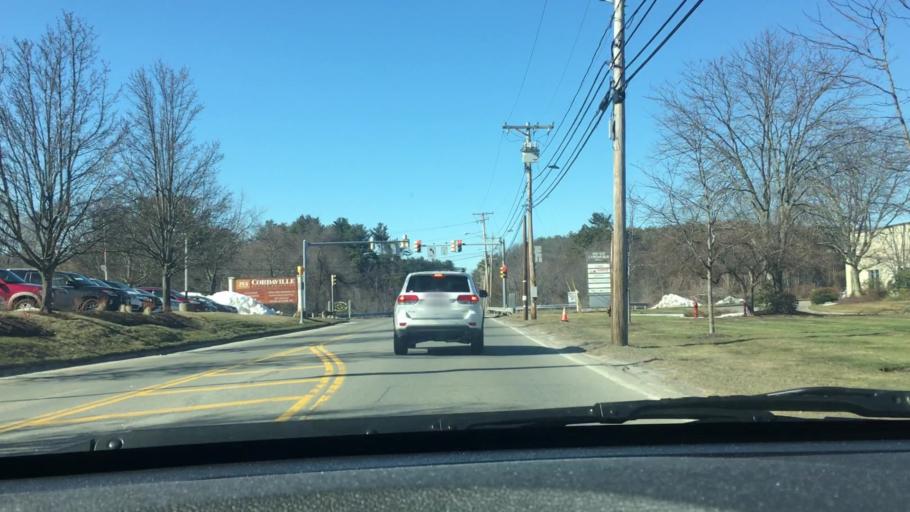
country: US
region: Massachusetts
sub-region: Worcester County
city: Southborough
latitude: 42.2881
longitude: -71.5262
